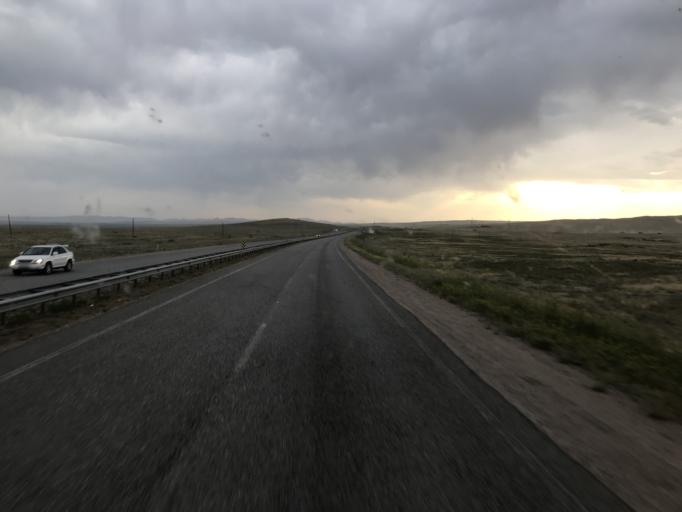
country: KZ
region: Zhambyl
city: Taraz
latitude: 42.7383
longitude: 70.9717
